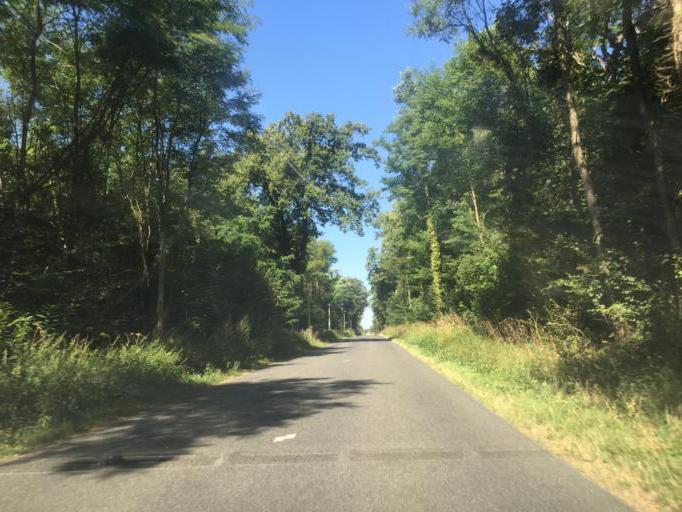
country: FR
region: Rhone-Alpes
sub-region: Departement de l'Ain
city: Tramoyes
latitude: 45.8996
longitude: 4.9662
